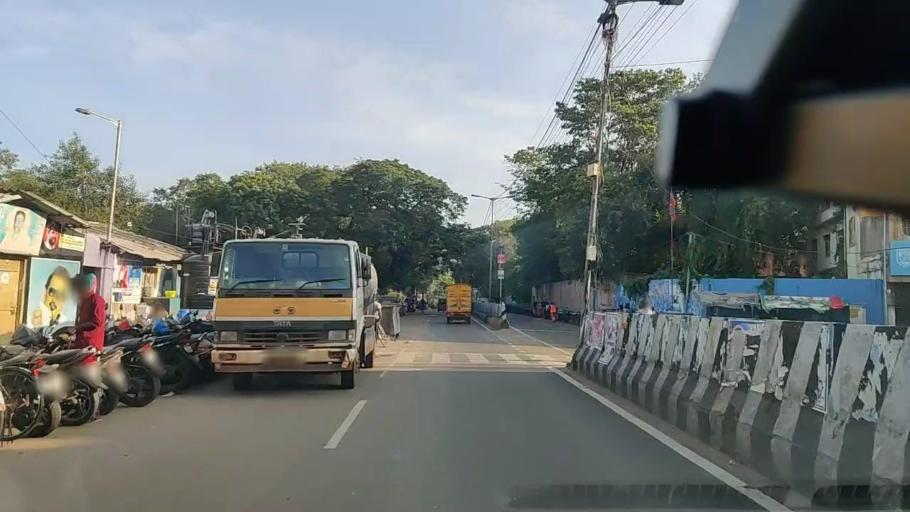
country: IN
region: Tamil Nadu
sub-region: Chennai
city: George Town
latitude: 13.0938
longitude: 80.2752
